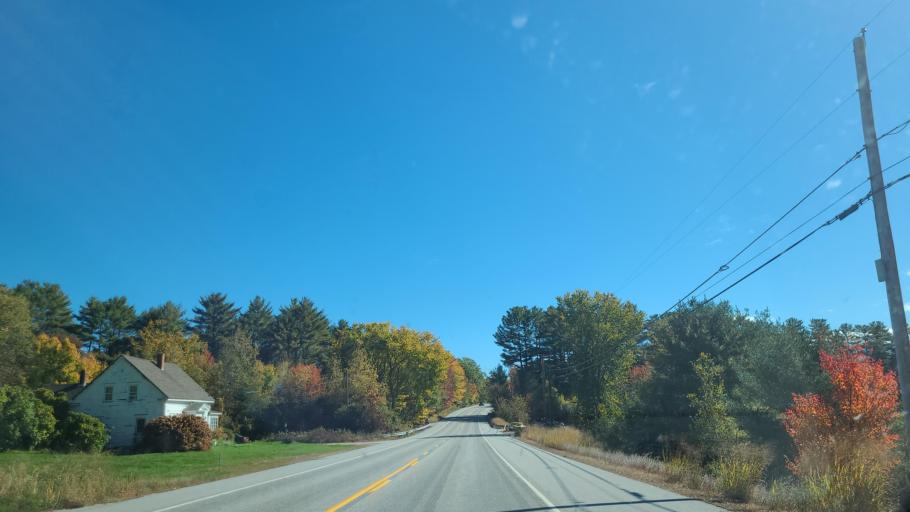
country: US
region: Maine
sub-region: Cumberland County
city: Bridgton
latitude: 44.0692
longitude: -70.7714
